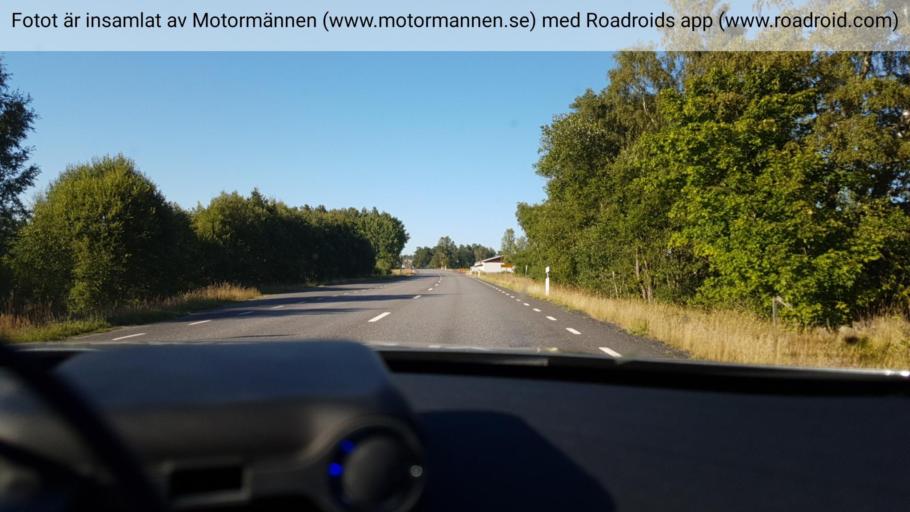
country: SE
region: Joenkoeping
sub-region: Habo Kommun
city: Habo
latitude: 57.9932
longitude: 14.1156
